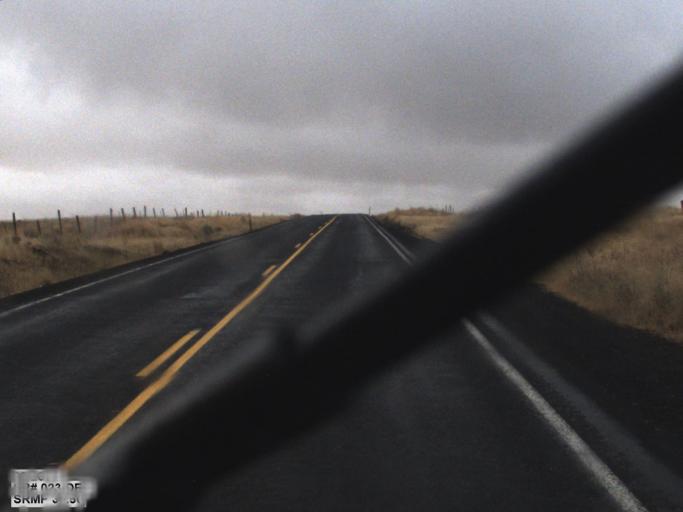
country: US
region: Washington
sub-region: Spokane County
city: Medical Lake
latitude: 47.2248
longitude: -117.9055
